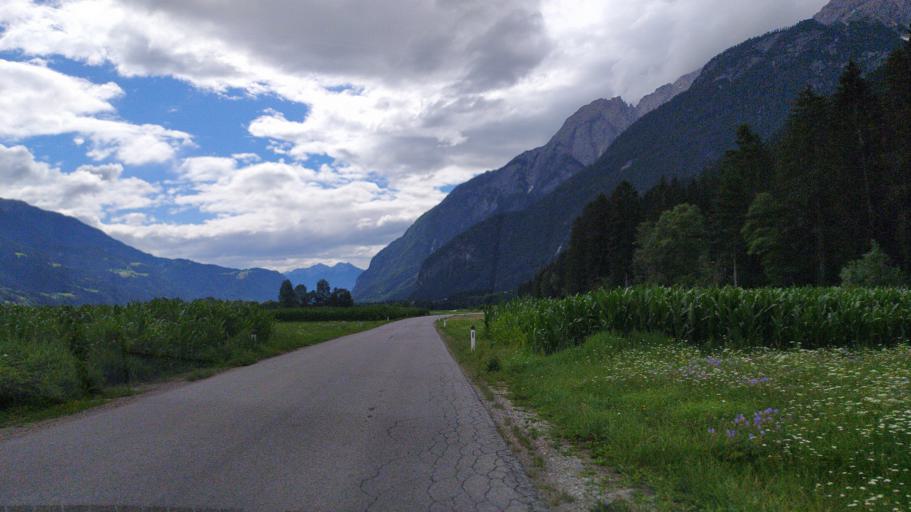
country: AT
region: Tyrol
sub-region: Politischer Bezirk Lienz
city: Lavant
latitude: 46.8095
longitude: 12.8219
